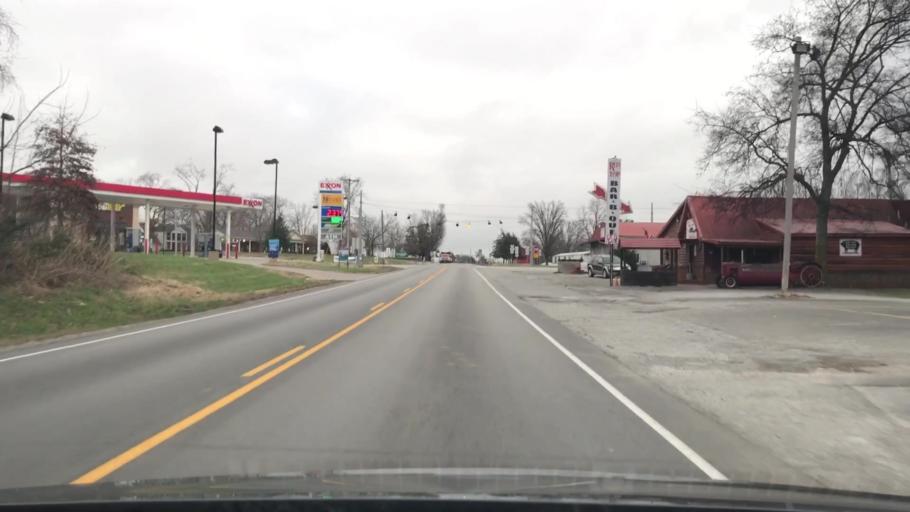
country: US
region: Kentucky
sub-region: Todd County
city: Guthrie
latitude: 36.6439
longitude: -87.2009
